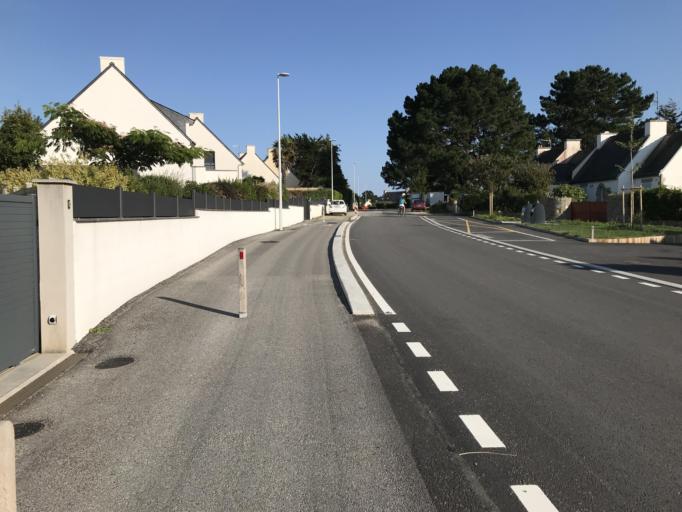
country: FR
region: Brittany
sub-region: Departement du Morbihan
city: Arzon
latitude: 47.5520
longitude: -2.8930
